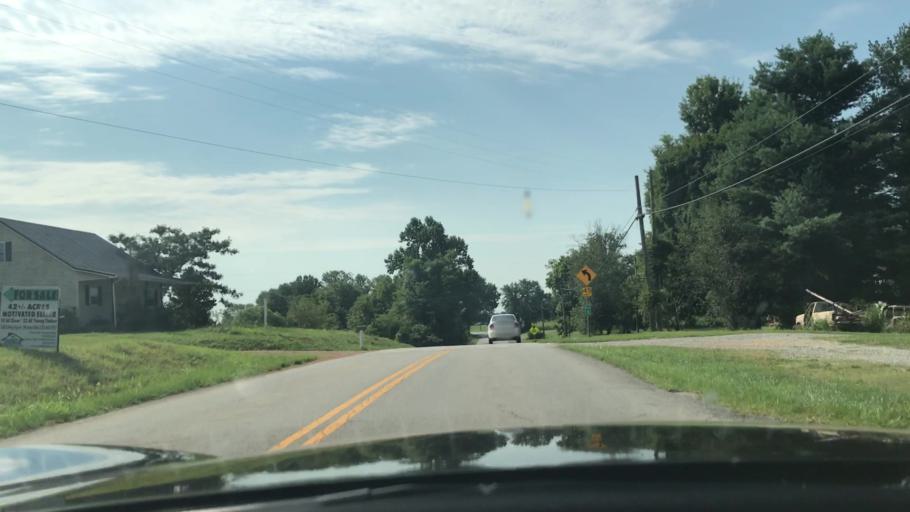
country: US
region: Kentucky
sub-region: Green County
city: Greensburg
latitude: 37.2643
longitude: -85.5606
